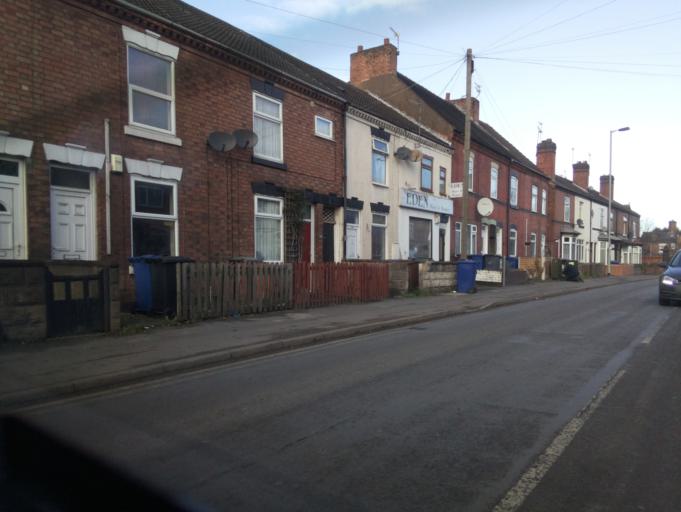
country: GB
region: England
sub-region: Staffordshire
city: Burton upon Trent
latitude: 52.7923
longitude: -1.6433
